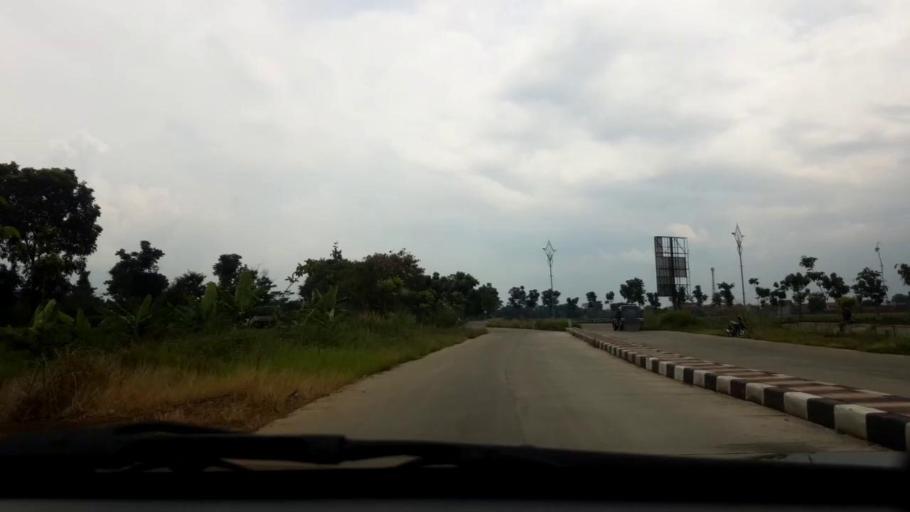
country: ID
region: West Java
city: Cileunyi
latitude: -6.9641
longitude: 107.7104
